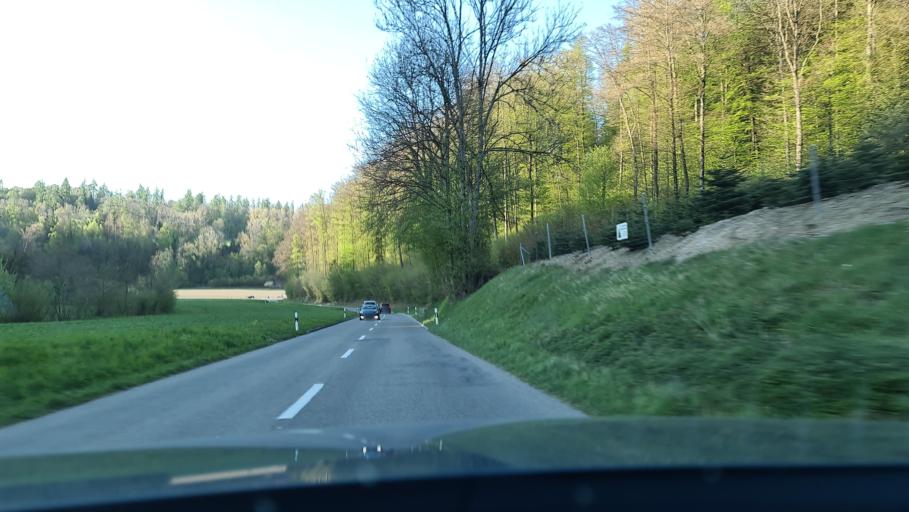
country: CH
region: Aargau
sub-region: Bezirk Lenzburg
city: Egliswil
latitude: 47.3652
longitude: 8.1989
